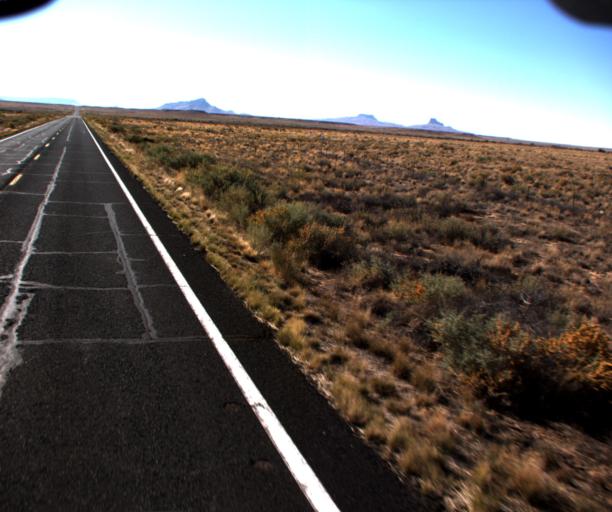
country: US
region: Arizona
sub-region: Navajo County
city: Dilkon
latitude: 35.5796
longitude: -110.4634
